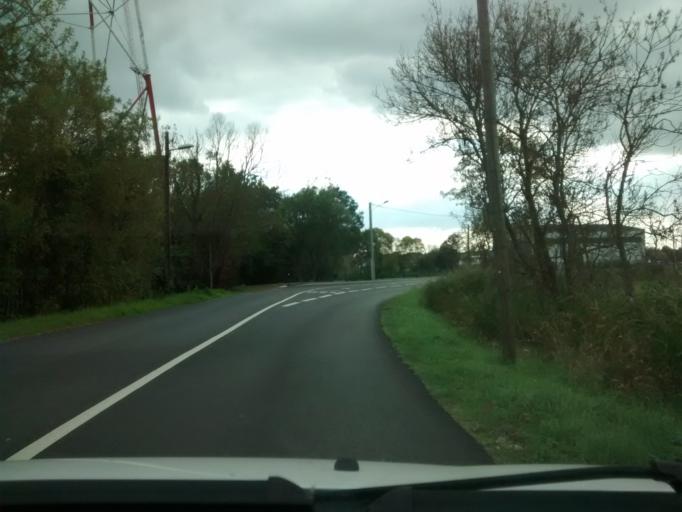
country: FR
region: Pays de la Loire
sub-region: Departement de la Loire-Atlantique
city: Le Pellerin
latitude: 47.2072
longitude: -1.7496
